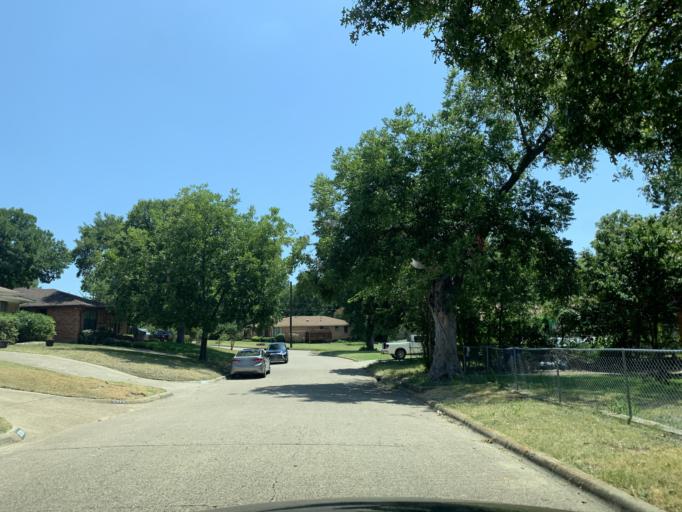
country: US
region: Texas
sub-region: Dallas County
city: Cockrell Hill
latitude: 32.6802
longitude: -96.8097
